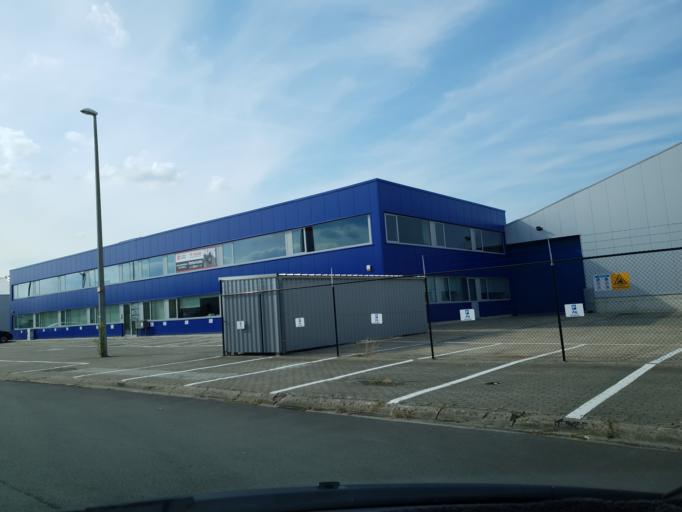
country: BE
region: Flanders
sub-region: Provincie Antwerpen
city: Antwerpen
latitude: 51.2719
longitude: 4.3934
